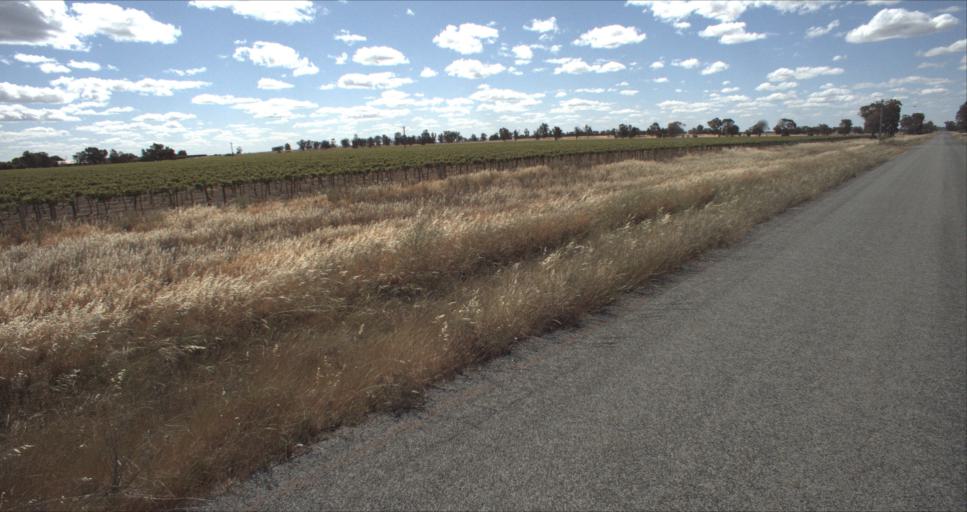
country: AU
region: New South Wales
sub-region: Leeton
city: Leeton
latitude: -34.4959
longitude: 146.2464
